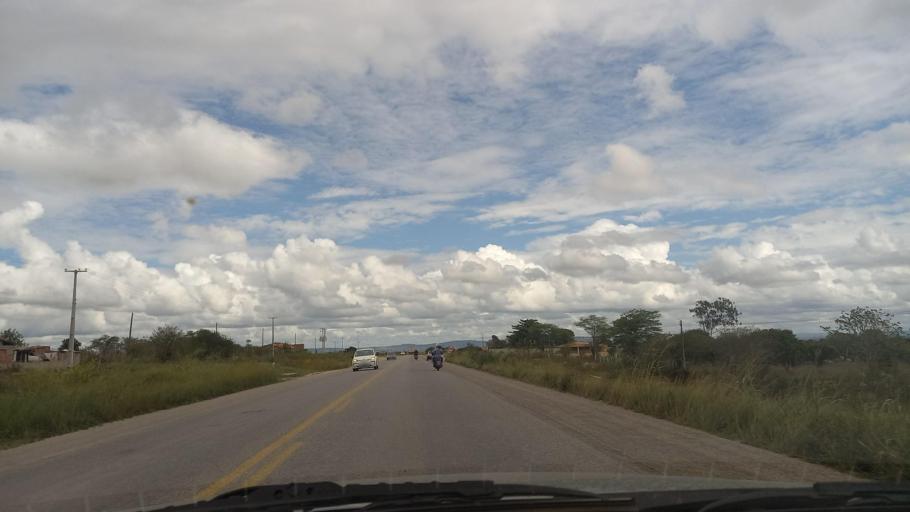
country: BR
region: Pernambuco
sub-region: Cachoeirinha
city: Cachoeirinha
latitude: -8.3732
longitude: -36.1727
